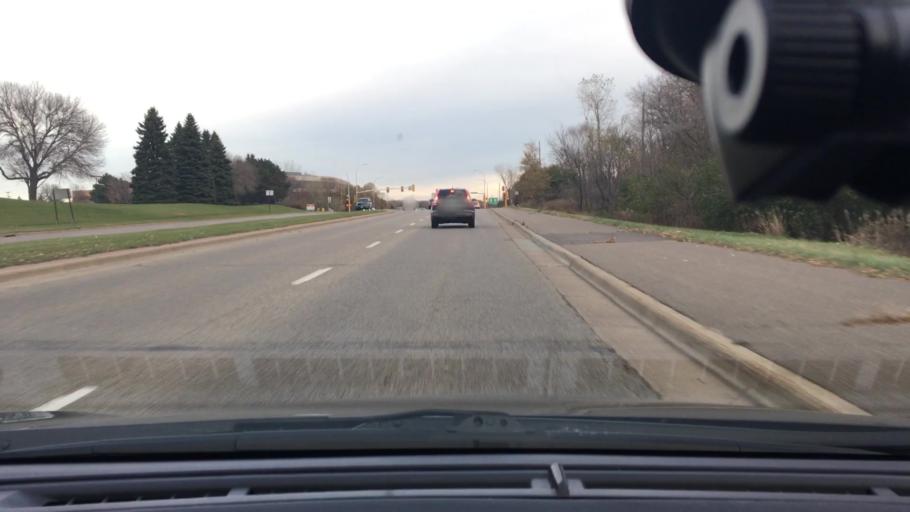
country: US
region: Minnesota
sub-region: Hennepin County
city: New Hope
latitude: 45.0584
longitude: -93.4112
